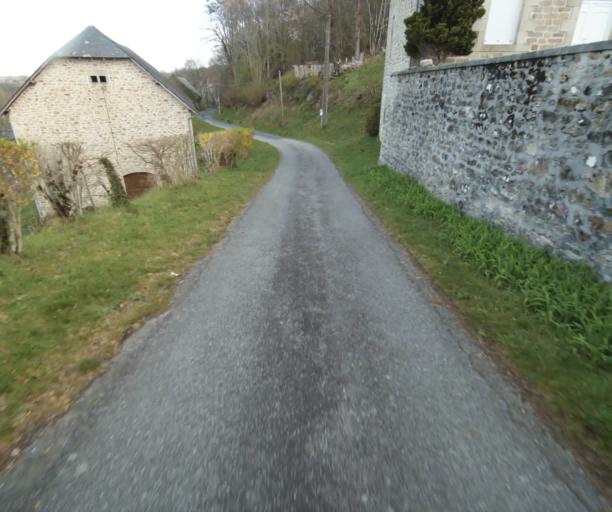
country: FR
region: Limousin
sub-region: Departement de la Correze
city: Correze
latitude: 45.3638
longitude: 1.8517
